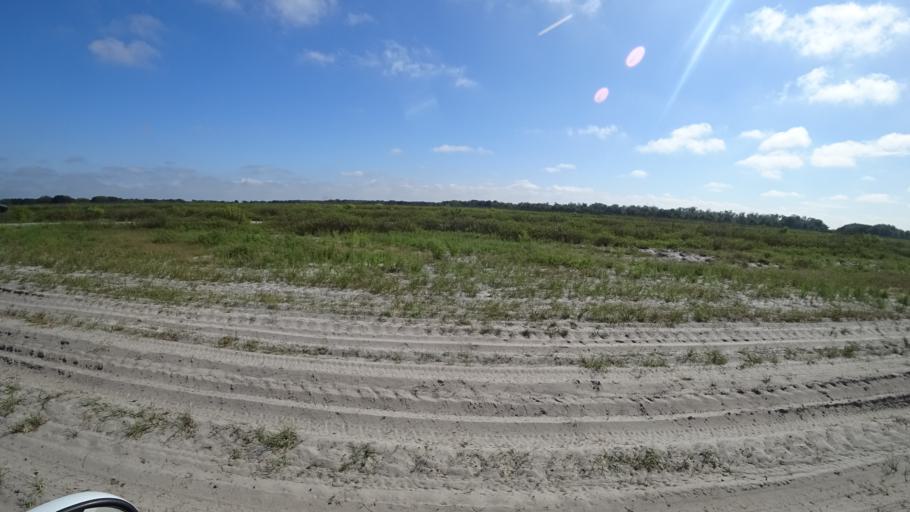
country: US
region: Florida
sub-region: DeSoto County
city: Arcadia
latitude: 27.2908
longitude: -82.0764
